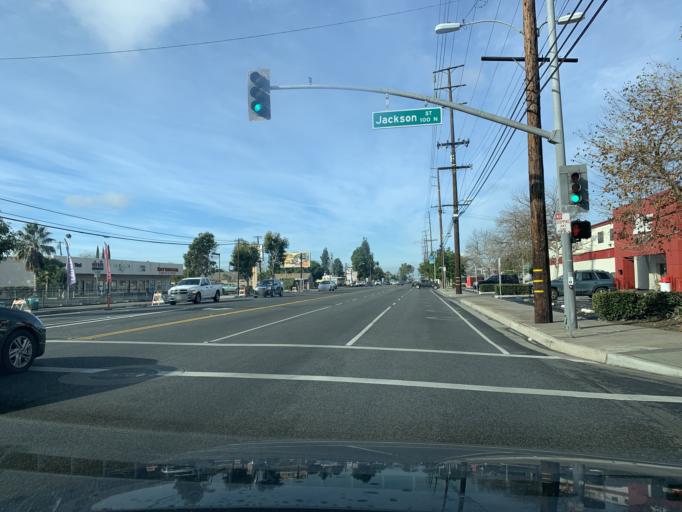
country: US
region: California
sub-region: Orange County
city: Garden Grove
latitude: 33.7453
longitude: -117.9157
